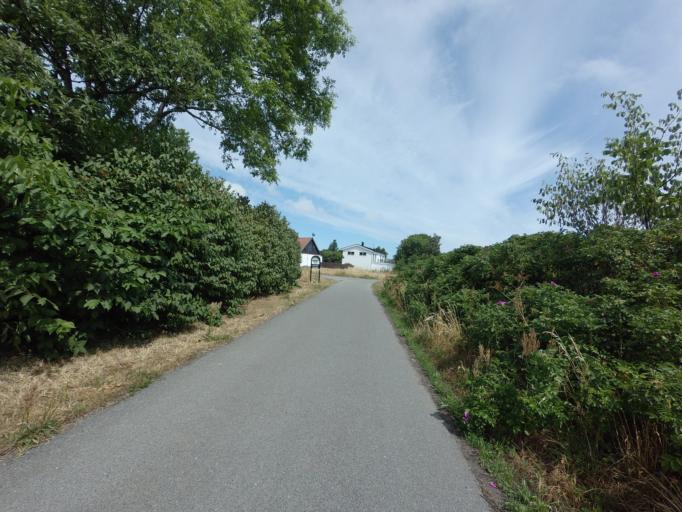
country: SE
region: Skane
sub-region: Simrishamns Kommun
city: Simrishamn
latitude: 55.5245
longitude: 14.3475
